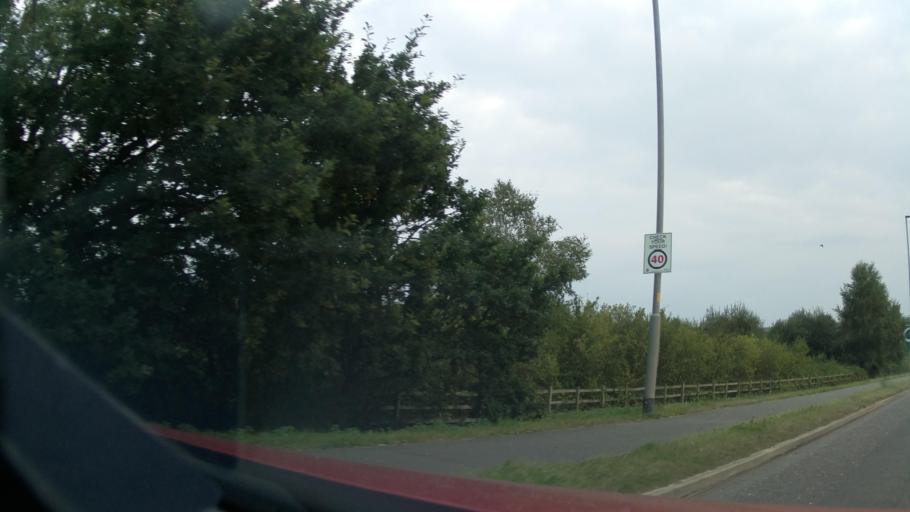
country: GB
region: England
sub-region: Lincolnshire
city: Skellingthorpe
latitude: 53.1537
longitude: -0.6712
